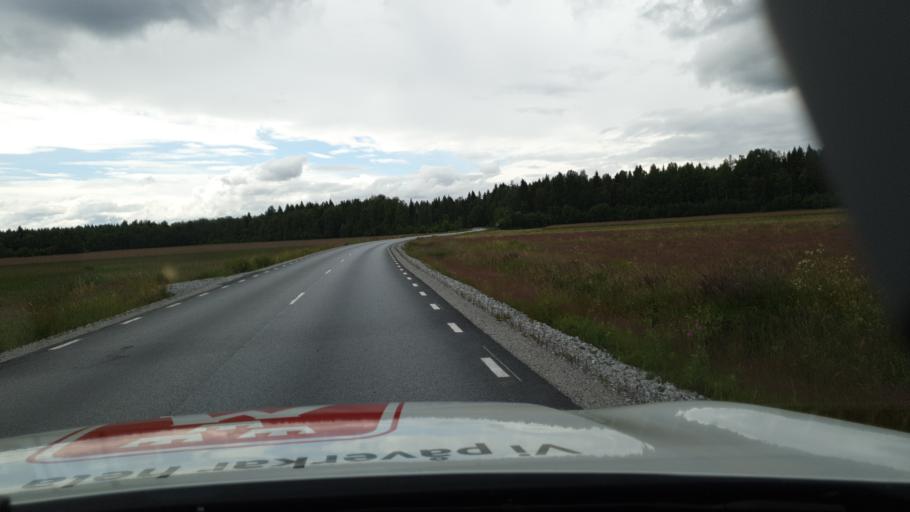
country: SE
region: Vaesterbotten
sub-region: Nordmalings Kommun
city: Nordmaling
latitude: 63.5743
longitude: 19.4309
